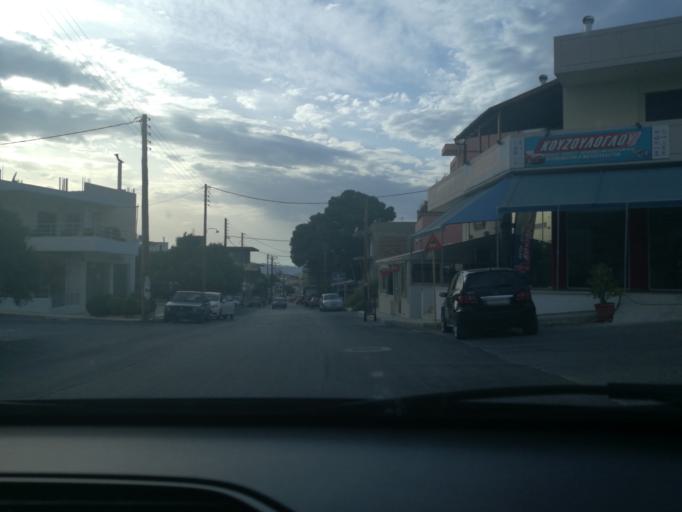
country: GR
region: Crete
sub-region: Nomos Irakleiou
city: Irakleion
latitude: 35.3155
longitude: 25.1389
